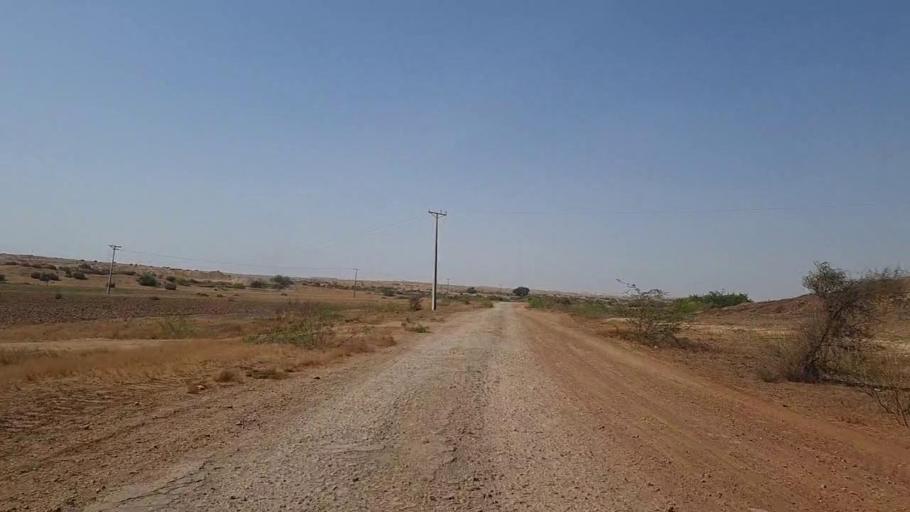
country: PK
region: Sindh
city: Kotri
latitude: 25.1637
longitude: 68.2010
